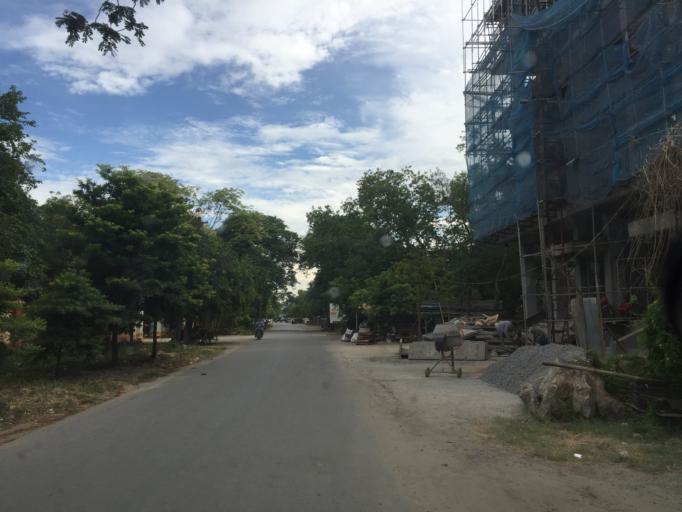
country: MM
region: Mandalay
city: Mandalay
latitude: 21.9730
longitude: 96.1047
